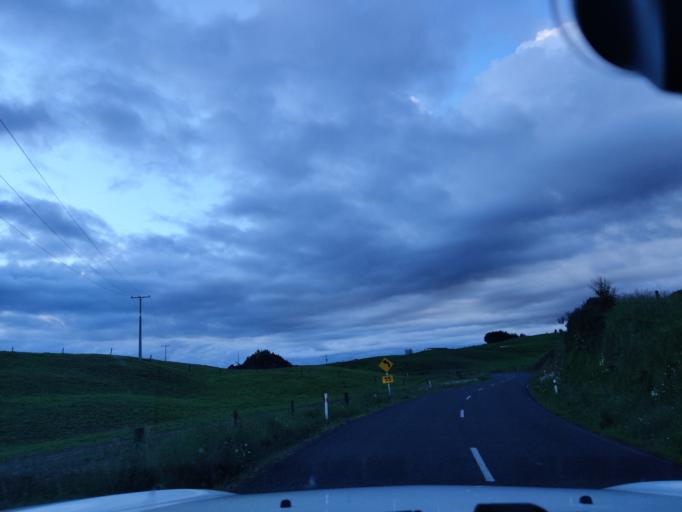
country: NZ
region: Waikato
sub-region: South Waikato District
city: Tokoroa
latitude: -38.1774
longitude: 175.7782
